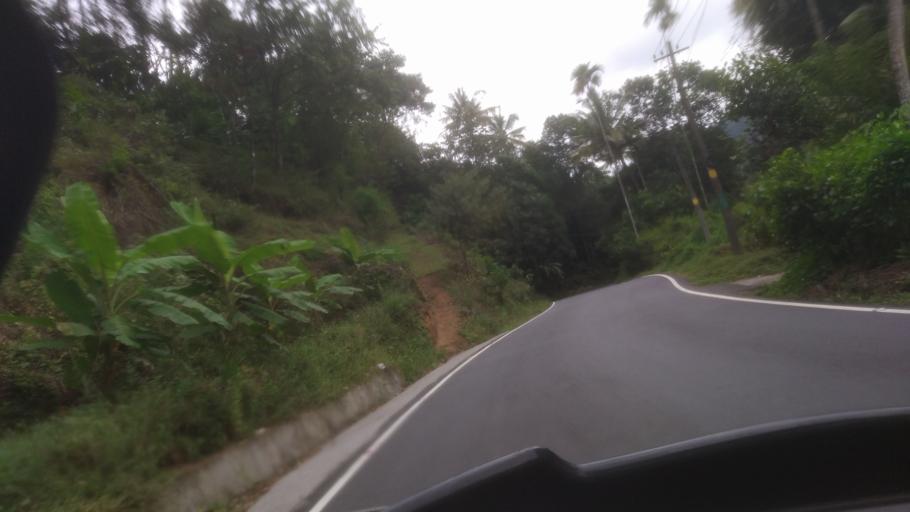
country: IN
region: Kerala
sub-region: Idukki
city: Idukki
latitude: 9.9692
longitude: 76.9999
